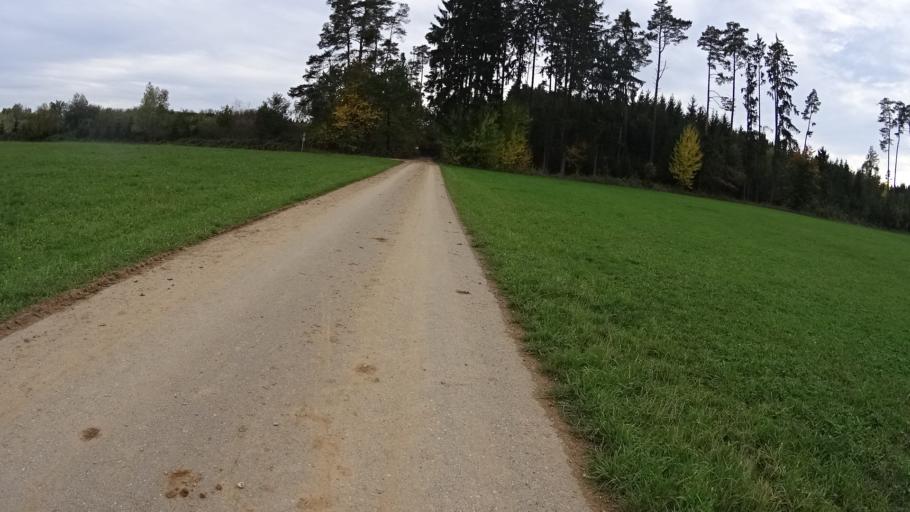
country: DE
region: Bavaria
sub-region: Upper Bavaria
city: Hitzhofen
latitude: 48.8521
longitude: 11.2995
